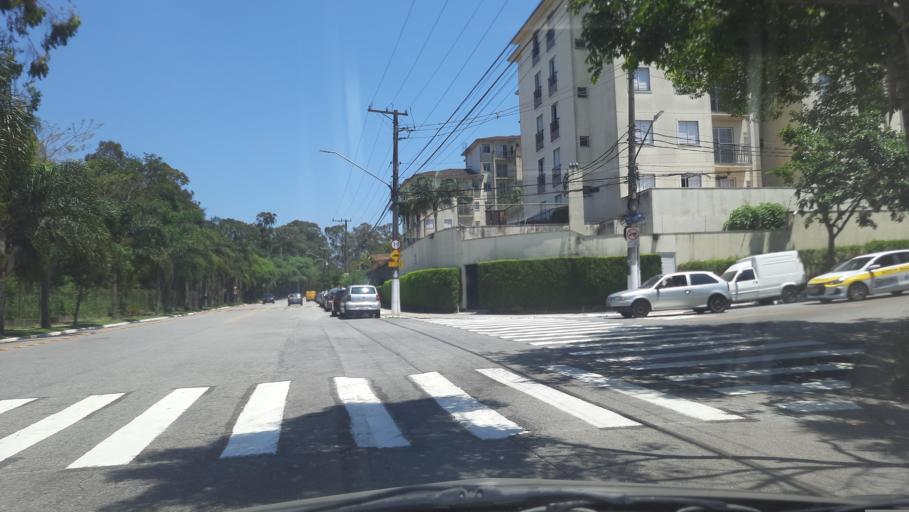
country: BR
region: Sao Paulo
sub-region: Caieiras
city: Caieiras
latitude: -23.4439
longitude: -46.7285
